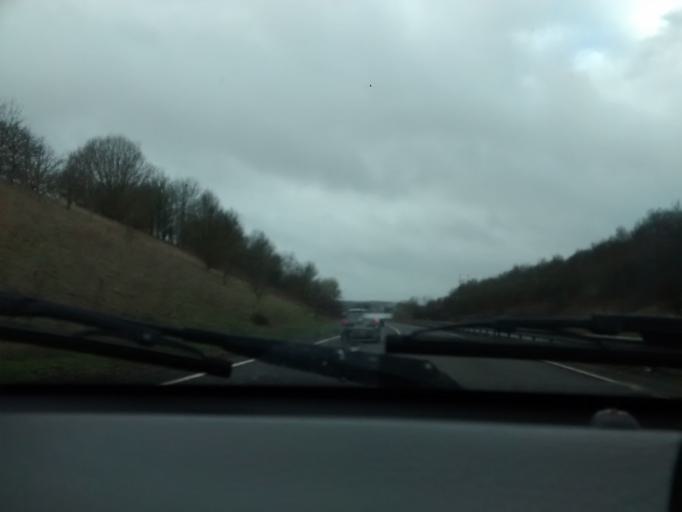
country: GB
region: England
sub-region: Suffolk
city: Stowmarket
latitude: 52.1966
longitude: 1.0054
